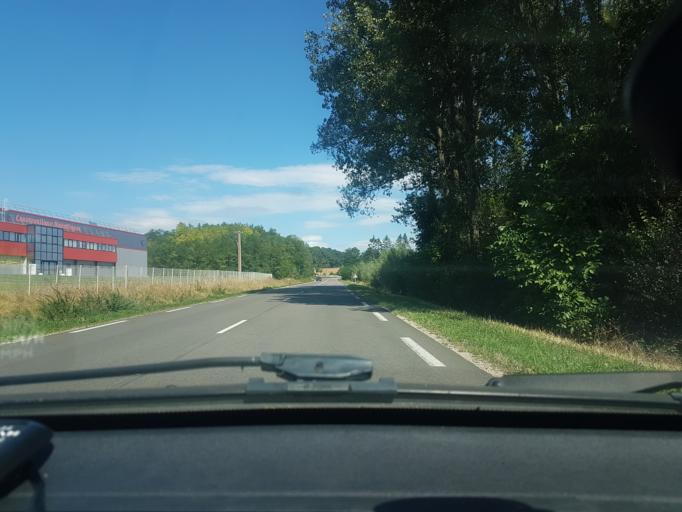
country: FR
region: Franche-Comte
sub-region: Departement de la Haute-Saone
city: Gray-la-Ville
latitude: 47.4427
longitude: 5.5491
